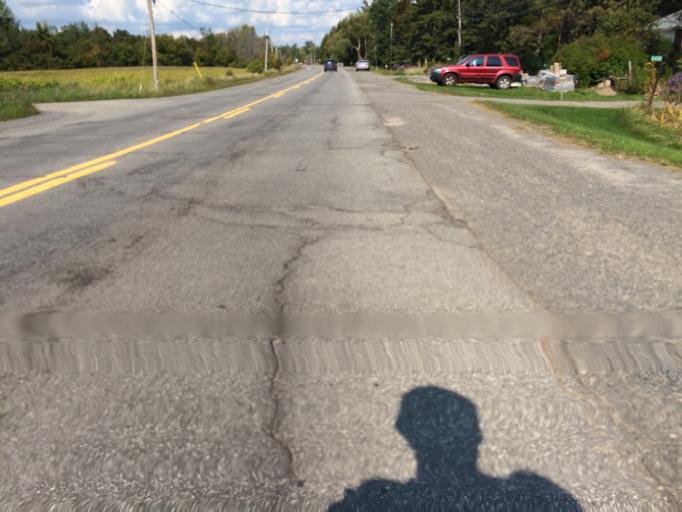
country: CA
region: Ontario
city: Bells Corners
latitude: 45.1703
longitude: -75.6403
